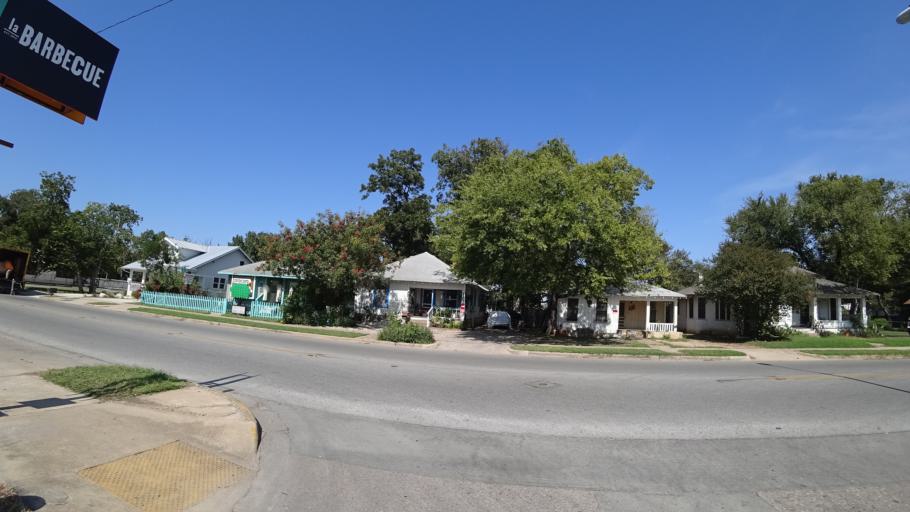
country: US
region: Texas
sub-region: Travis County
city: Austin
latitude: 30.2561
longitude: -97.7221
